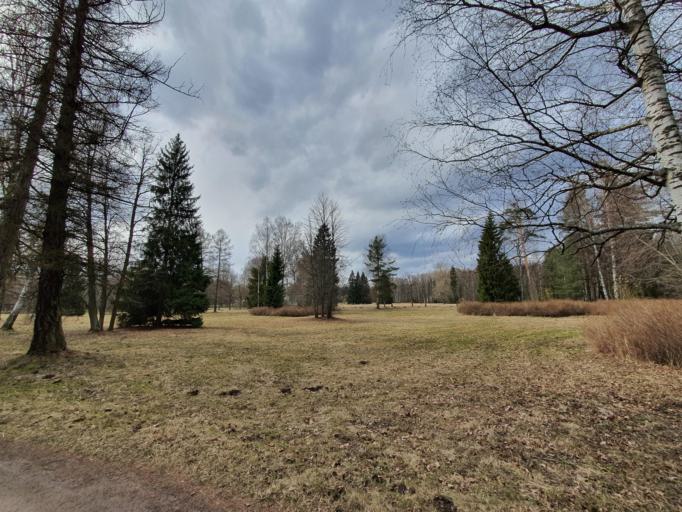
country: RU
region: St.-Petersburg
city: Tyarlevo
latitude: 59.6889
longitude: 30.4523
